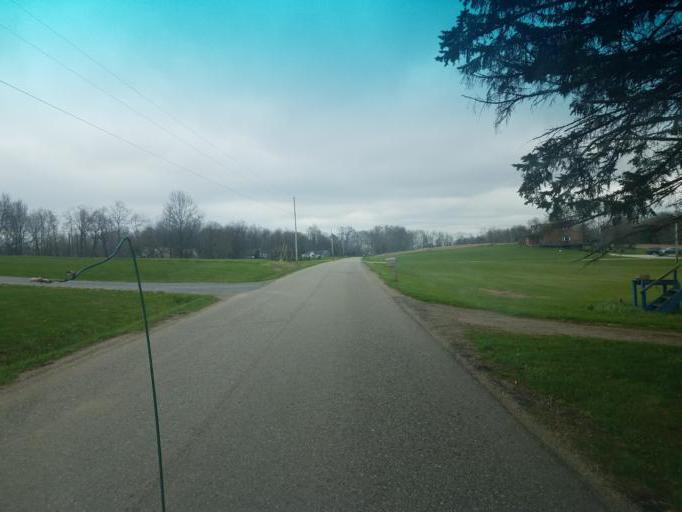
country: US
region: Ohio
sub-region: Stark County
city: Beach City
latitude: 40.6356
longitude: -81.6012
